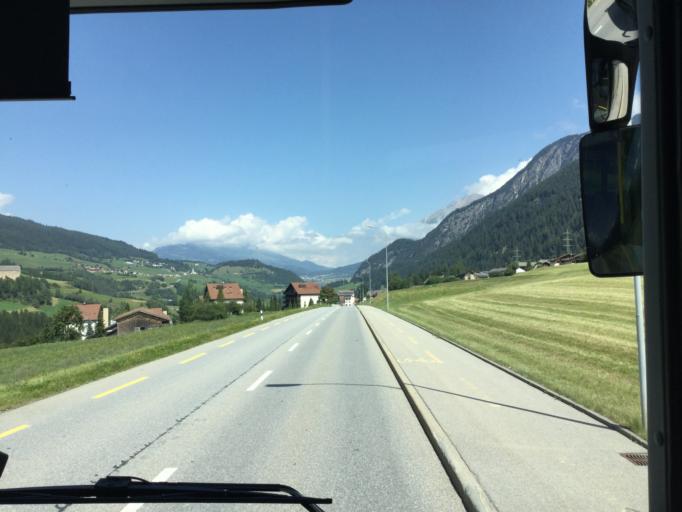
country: CH
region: Grisons
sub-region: Albula District
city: Tiefencastel
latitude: 46.6017
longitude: 9.5932
